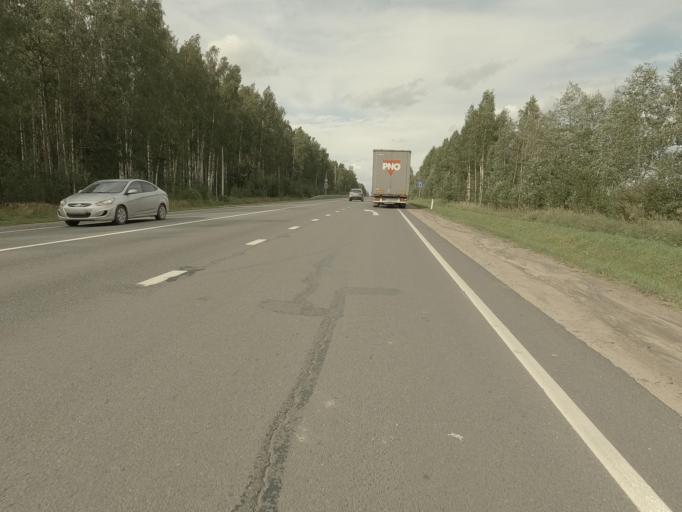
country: RU
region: Leningrad
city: Mga
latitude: 59.7862
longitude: 31.1063
